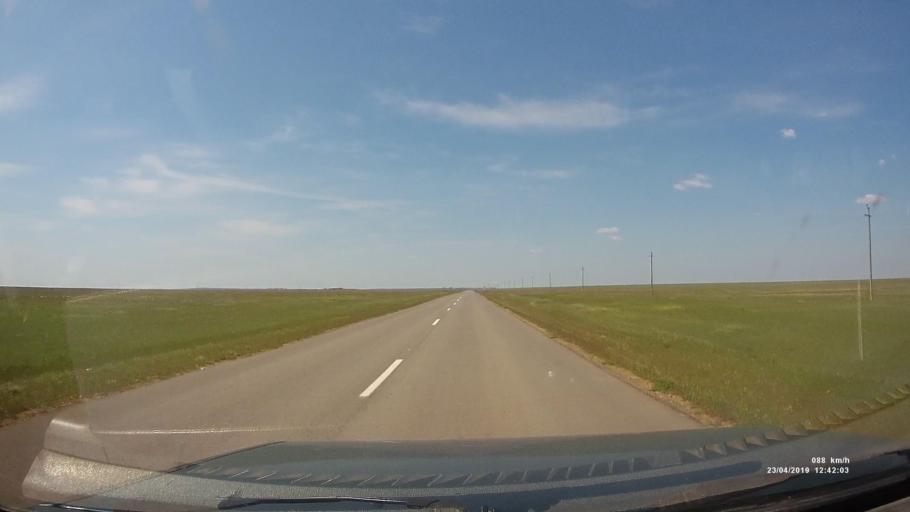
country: RU
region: Kalmykiya
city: Yashalta
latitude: 46.4529
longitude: 42.6717
